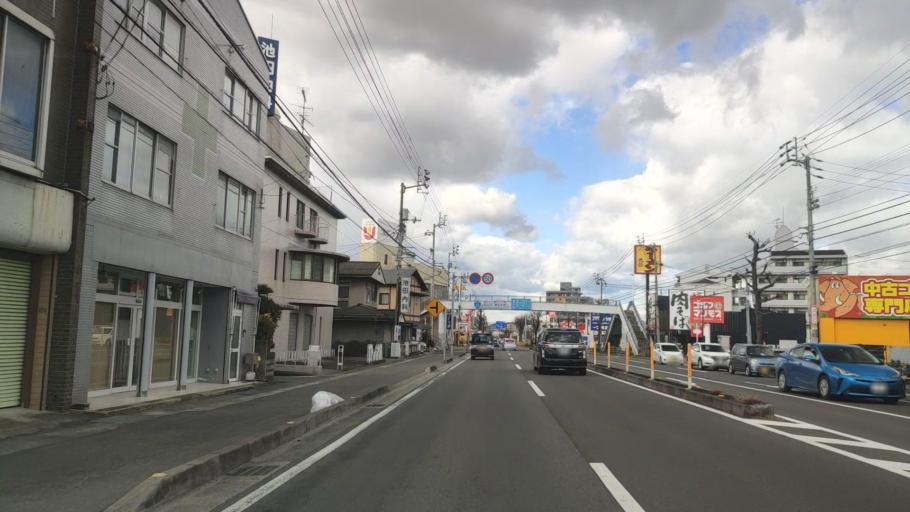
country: JP
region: Ehime
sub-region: Shikoku-chuo Shi
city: Matsuyama
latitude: 33.8096
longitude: 132.7799
